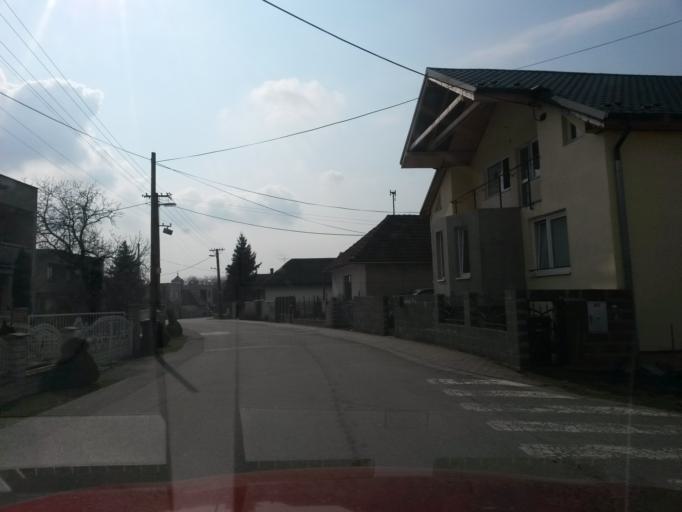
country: SK
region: Kosicky
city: Kosice
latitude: 48.6324
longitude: 21.1676
